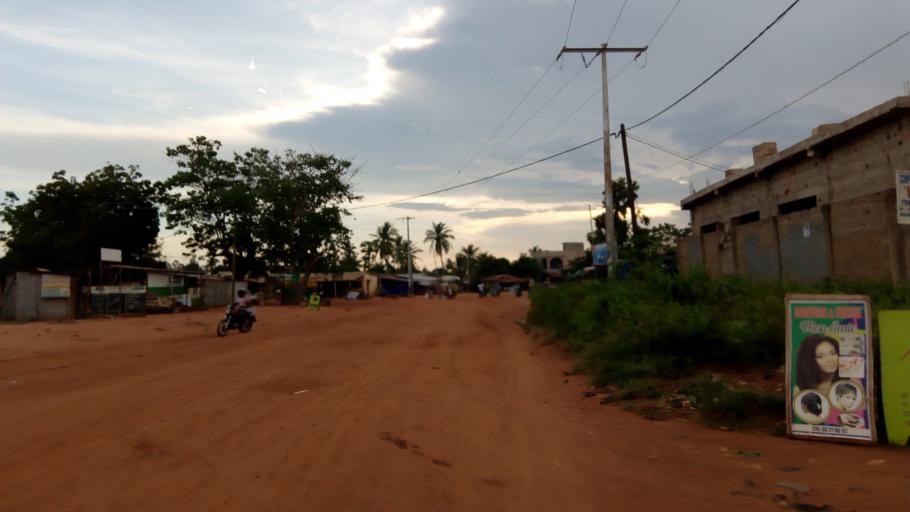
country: TG
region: Maritime
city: Lome
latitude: 6.2616
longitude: 1.1395
